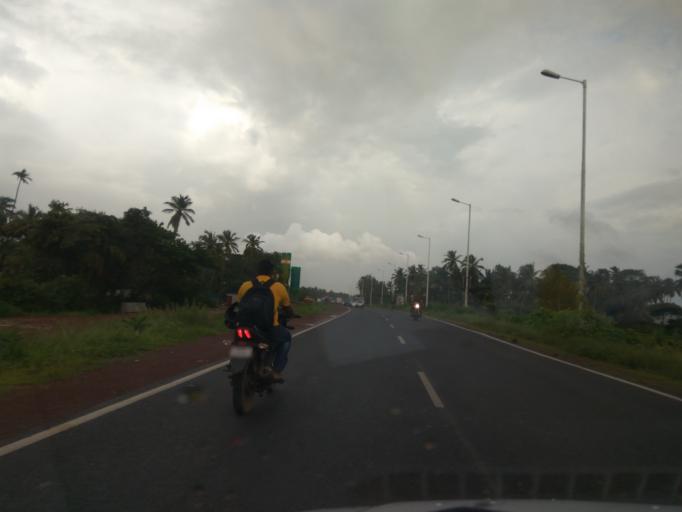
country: IN
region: Goa
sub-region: North Goa
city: Goa Velha
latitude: 15.4340
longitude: 73.8853
